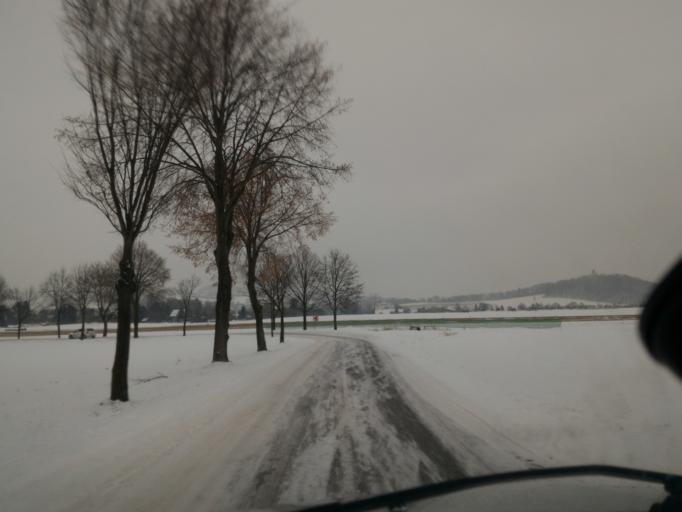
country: DE
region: Saxony
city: Seifhennersdorf
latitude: 50.9319
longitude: 14.5968
